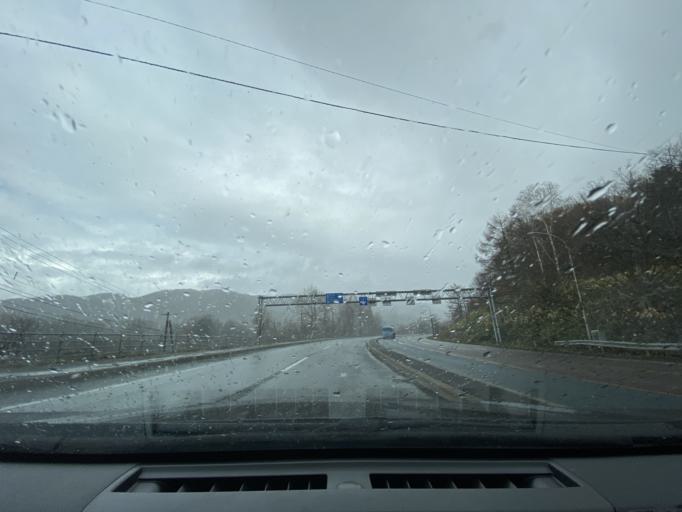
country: JP
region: Hokkaido
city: Fukagawa
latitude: 43.7279
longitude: 142.1876
